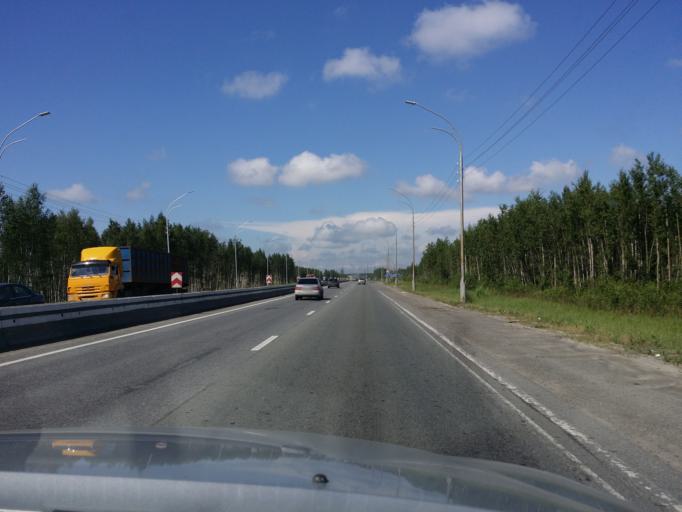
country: RU
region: Khanty-Mansiyskiy Avtonomnyy Okrug
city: Nizhnevartovsk
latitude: 60.9795
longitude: 76.5014
